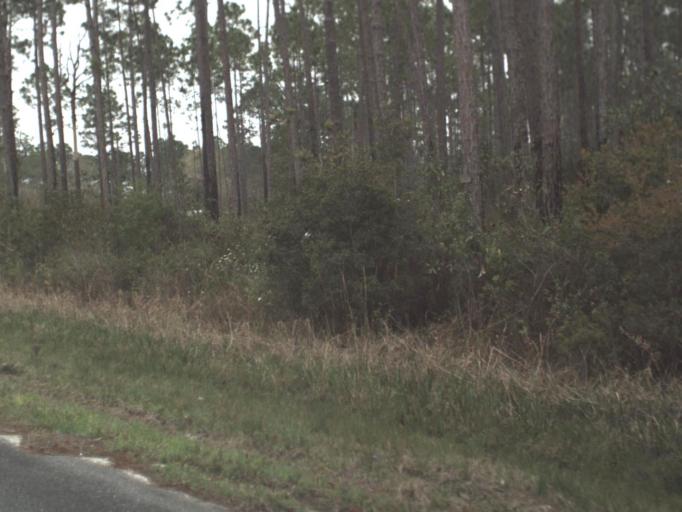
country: US
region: Florida
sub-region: Franklin County
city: Eastpoint
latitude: 29.8279
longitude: -84.8592
